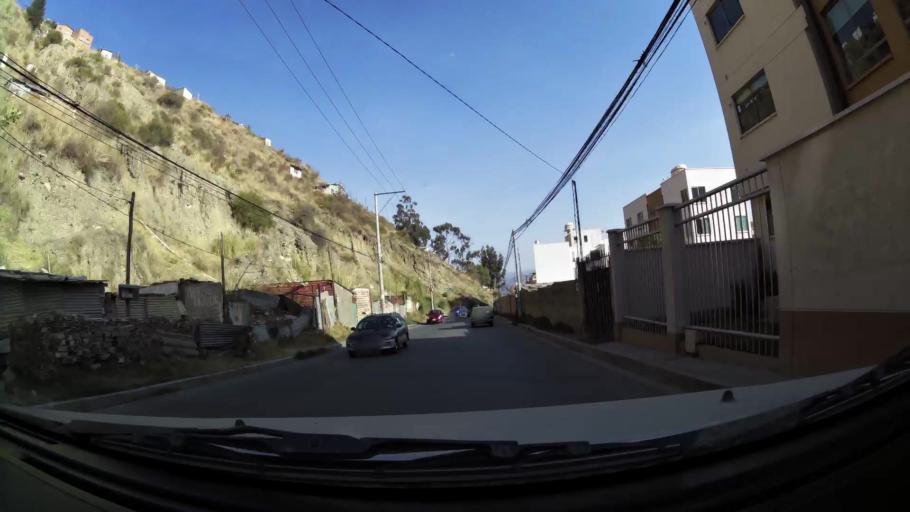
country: BO
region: La Paz
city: La Paz
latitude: -16.5101
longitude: -68.0855
